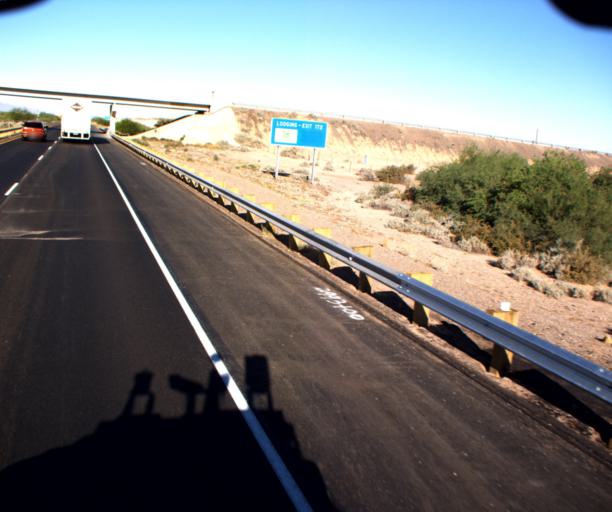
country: US
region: Arizona
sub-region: Pinal County
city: Casa Grande
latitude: 32.8282
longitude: -111.7563
